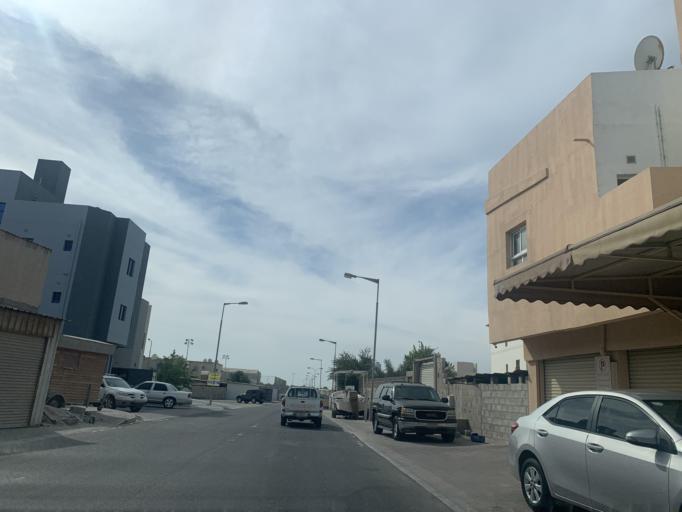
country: BH
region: Central Governorate
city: Madinat Hamad
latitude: 26.1198
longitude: 50.4779
